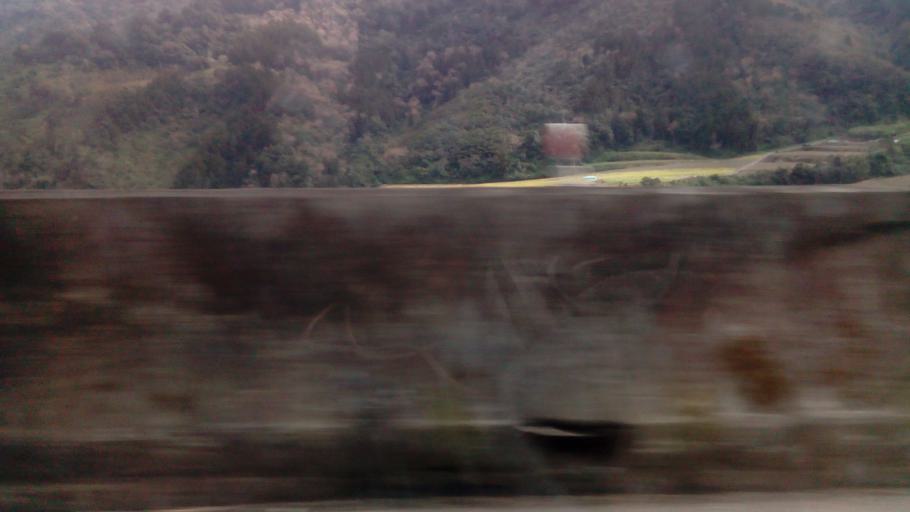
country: TW
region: Taiwan
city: Daxi
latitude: 24.4556
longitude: 121.3930
